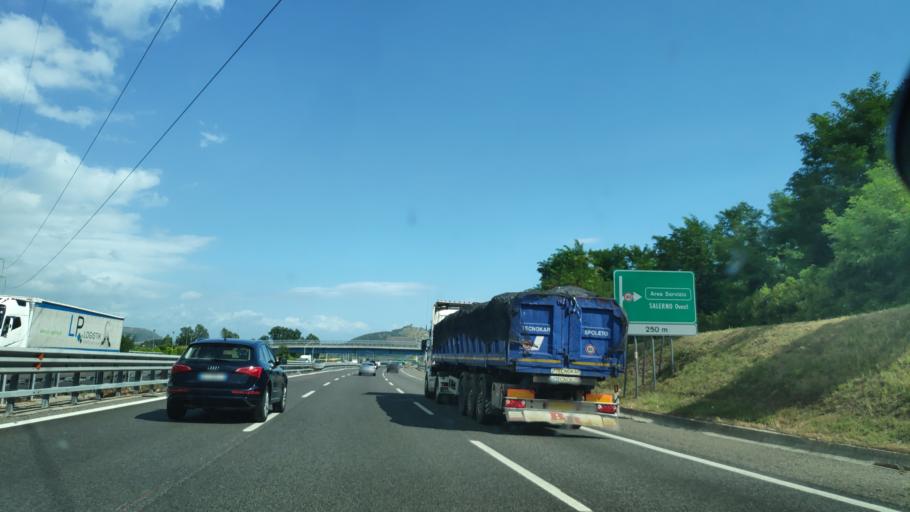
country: IT
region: Campania
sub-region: Provincia di Salerno
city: San Mango Piemonte
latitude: 40.6954
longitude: 14.8307
